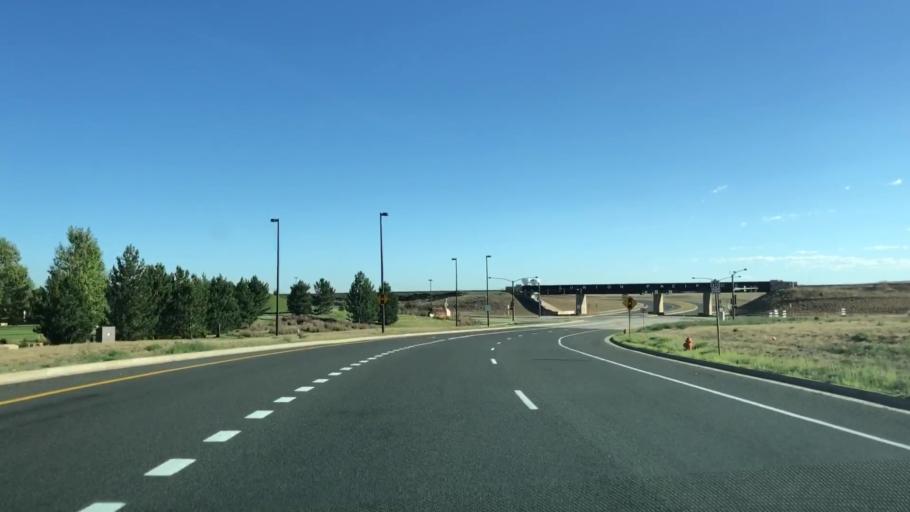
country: US
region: Colorado
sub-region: Larimer County
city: Loveland
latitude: 40.4148
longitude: -104.9862
